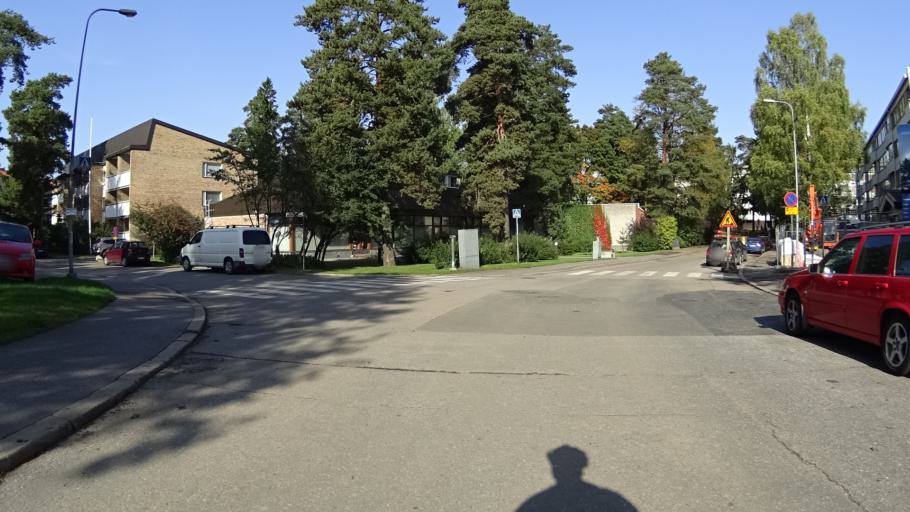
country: FI
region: Uusimaa
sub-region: Helsinki
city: Helsinki
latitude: 60.2091
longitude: 24.9034
